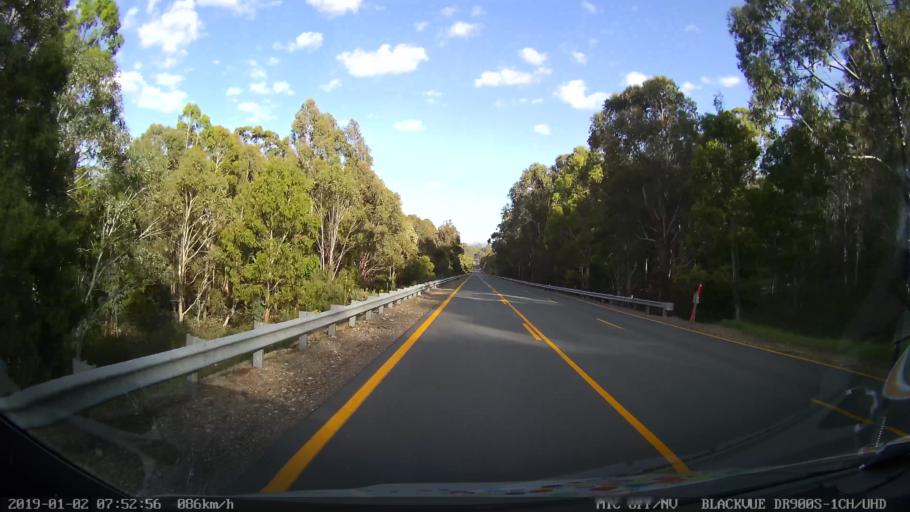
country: AU
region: New South Wales
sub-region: Tumut Shire
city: Tumut
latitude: -35.7110
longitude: 148.5124
